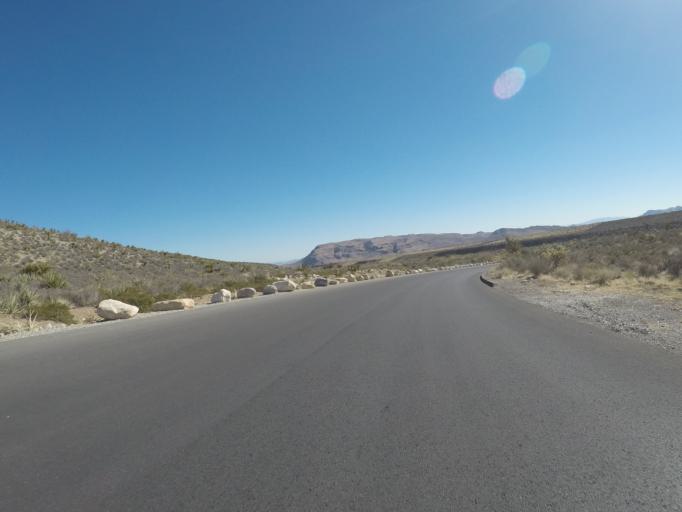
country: US
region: Nevada
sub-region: Clark County
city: Summerlin South
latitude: 36.1467
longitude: -115.4770
